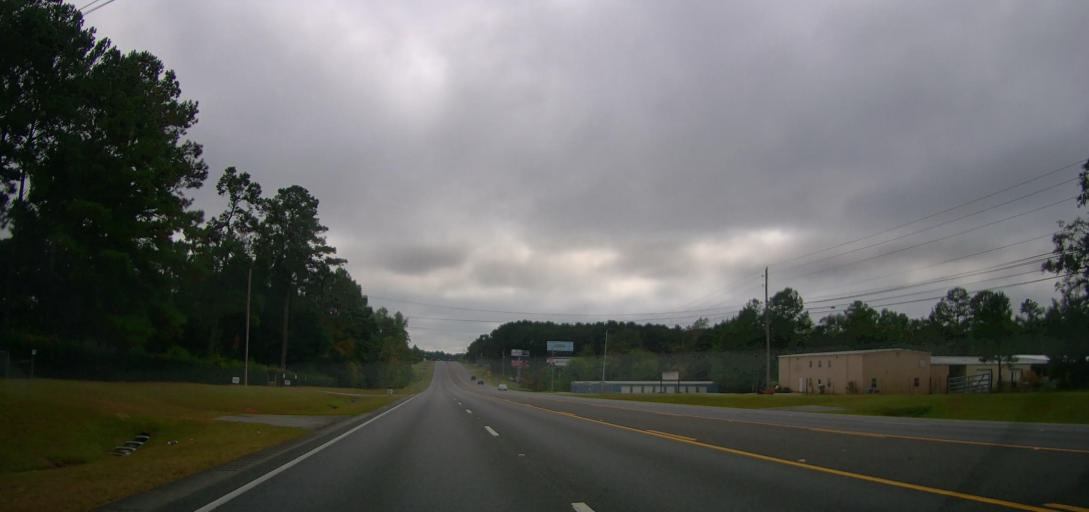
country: US
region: Georgia
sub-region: Thomas County
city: Thomasville
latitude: 30.8914
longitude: -83.9318
